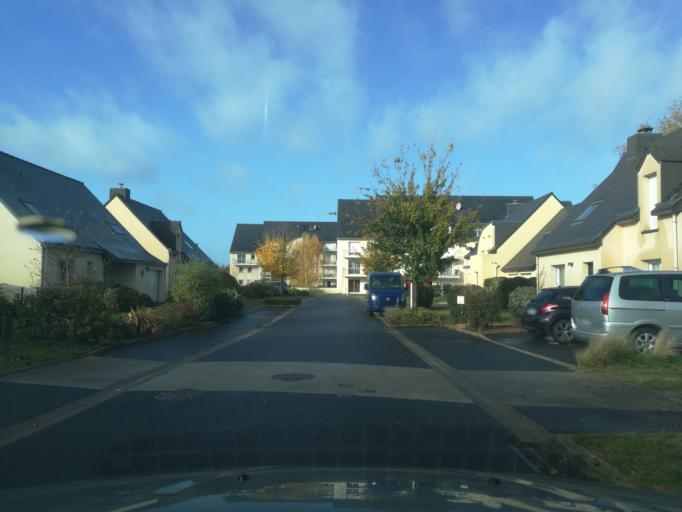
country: FR
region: Brittany
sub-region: Departement d'Ille-et-Vilaine
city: Pleumeleuc
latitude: 48.1827
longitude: -1.9250
